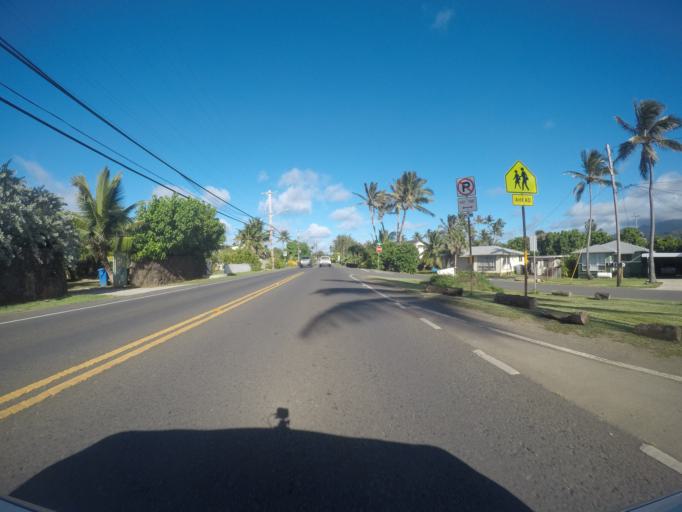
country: US
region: Hawaii
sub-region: Honolulu County
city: La'ie
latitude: 21.6513
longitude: -157.9268
